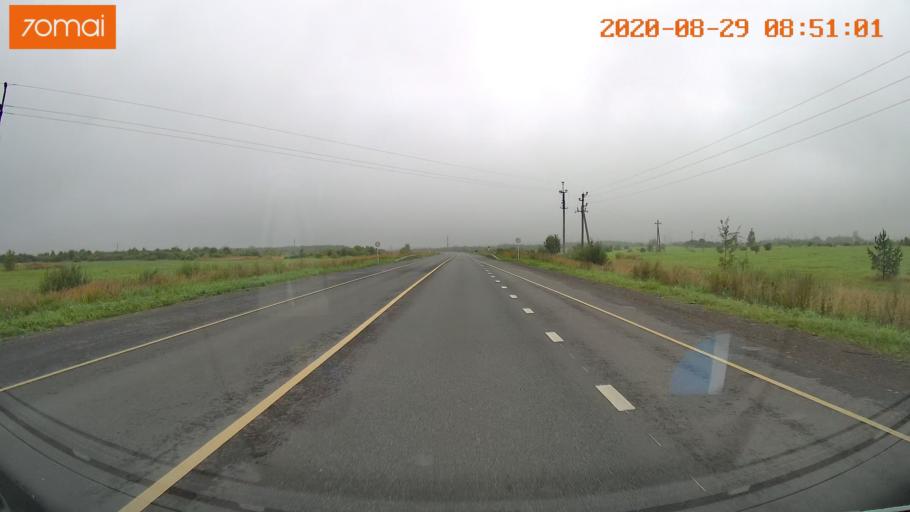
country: RU
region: Ivanovo
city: Vichuga
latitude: 57.1900
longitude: 41.8814
